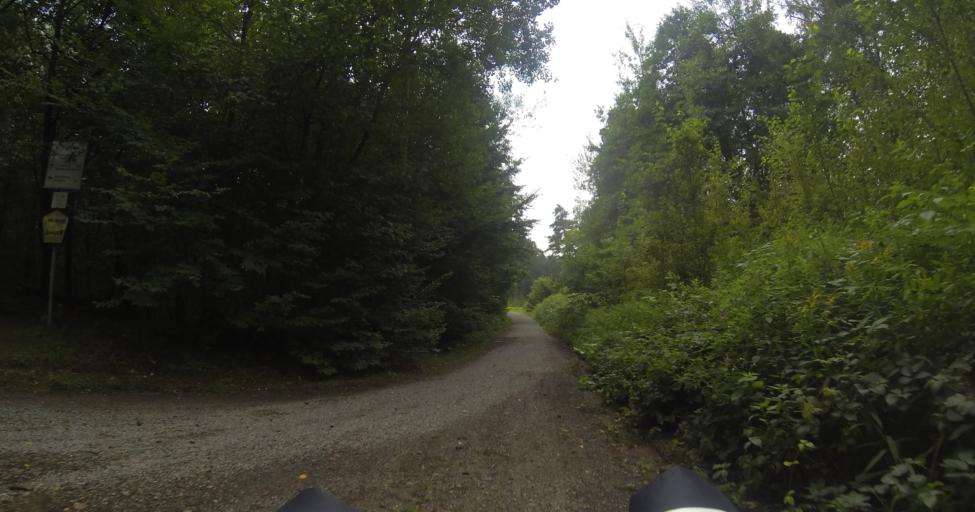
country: DE
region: Saxony
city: Coswig
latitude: 51.1650
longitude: 13.6164
